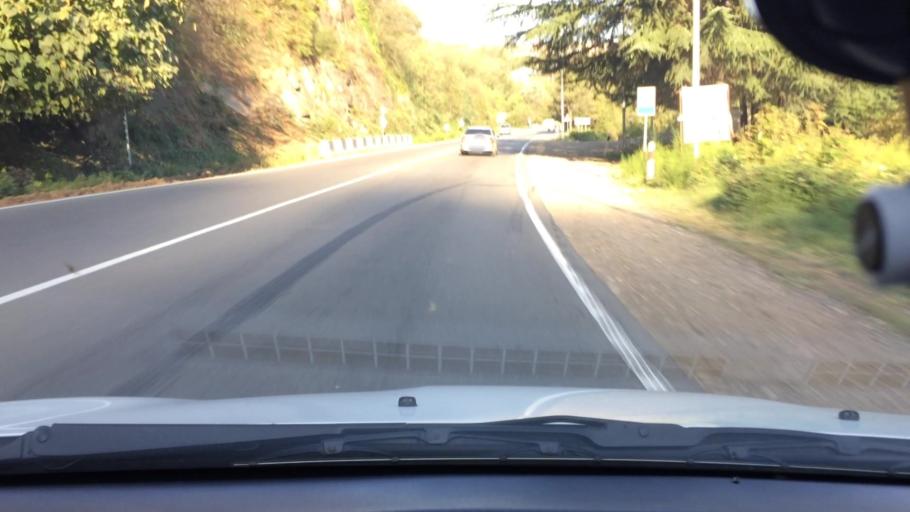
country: GE
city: Shorapani
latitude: 42.0921
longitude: 43.0802
